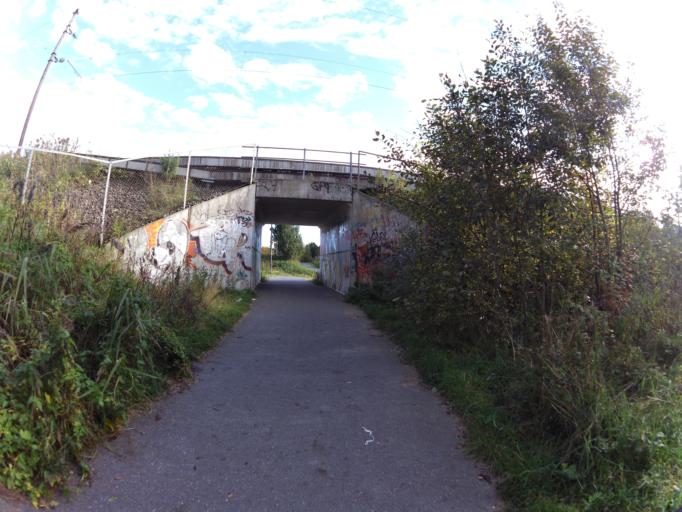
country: NO
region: Ostfold
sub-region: Sarpsborg
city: Sarpsborg
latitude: 59.2860
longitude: 11.0943
